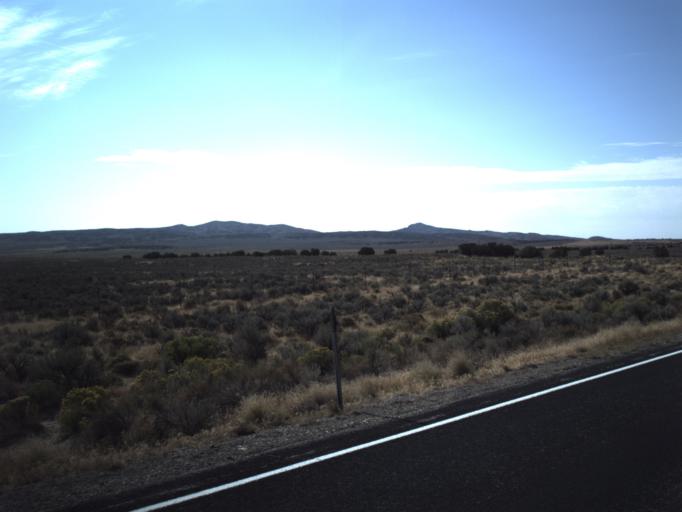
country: US
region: Idaho
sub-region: Cassia County
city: Burley
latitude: 41.7201
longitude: -113.5268
